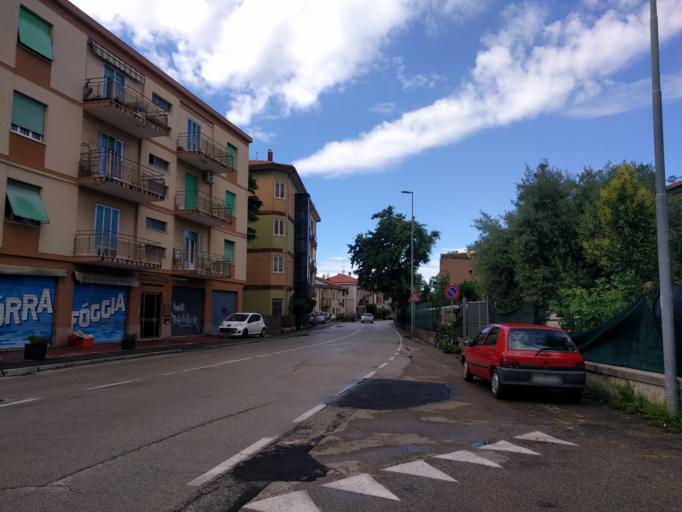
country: IT
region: The Marches
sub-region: Provincia di Pesaro e Urbino
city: Pesaro
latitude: 43.8984
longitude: 12.9073
